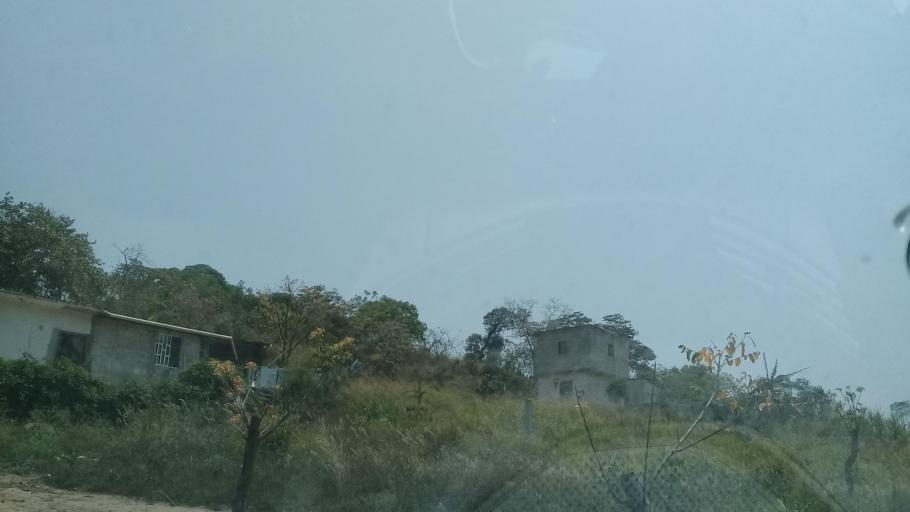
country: MX
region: Veracruz
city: El Castillo
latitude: 19.5658
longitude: -96.8447
